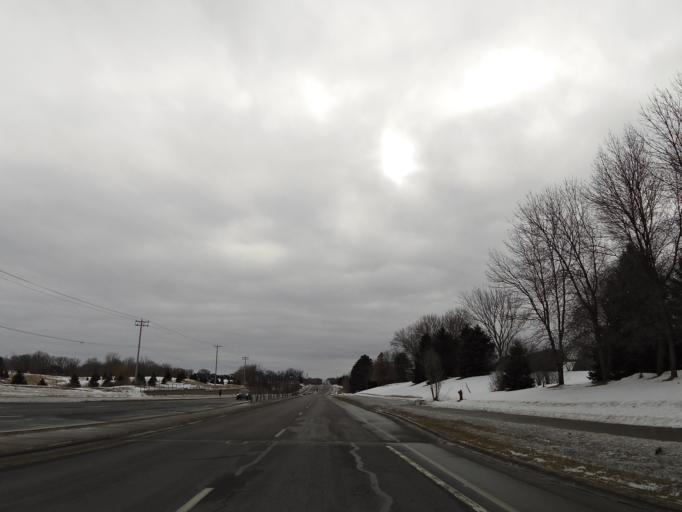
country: US
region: Minnesota
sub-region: Washington County
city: Woodbury
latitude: 44.9150
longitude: -92.9035
